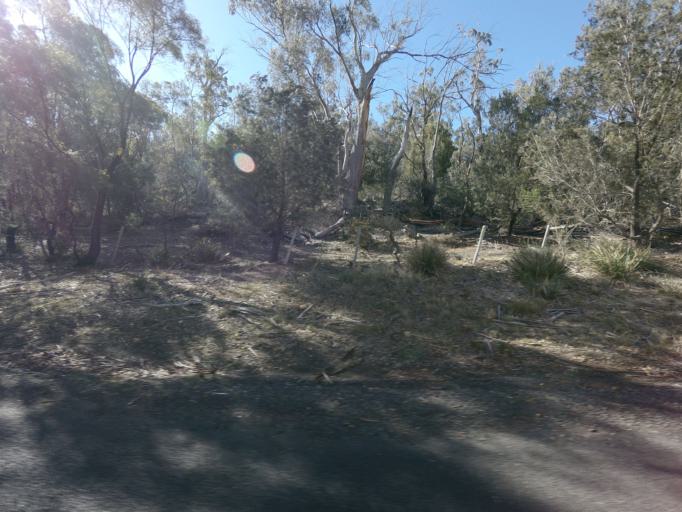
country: AU
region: Tasmania
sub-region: Sorell
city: Sorell
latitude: -42.3613
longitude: 147.9452
